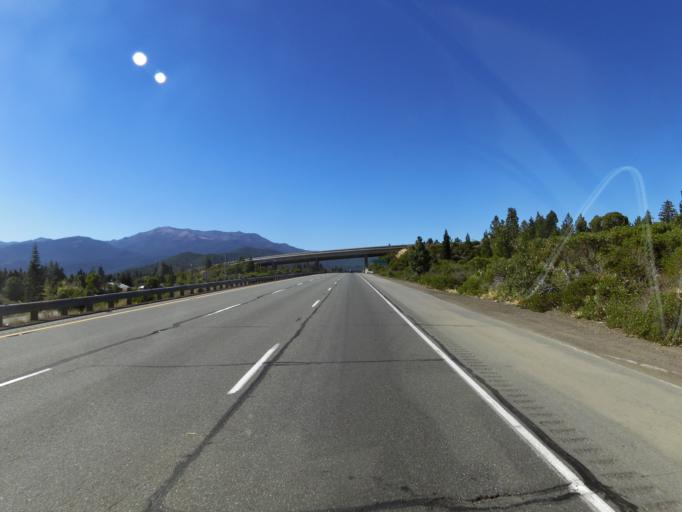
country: US
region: California
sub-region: Siskiyou County
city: Mount Shasta
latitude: 41.2839
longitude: -122.2998
